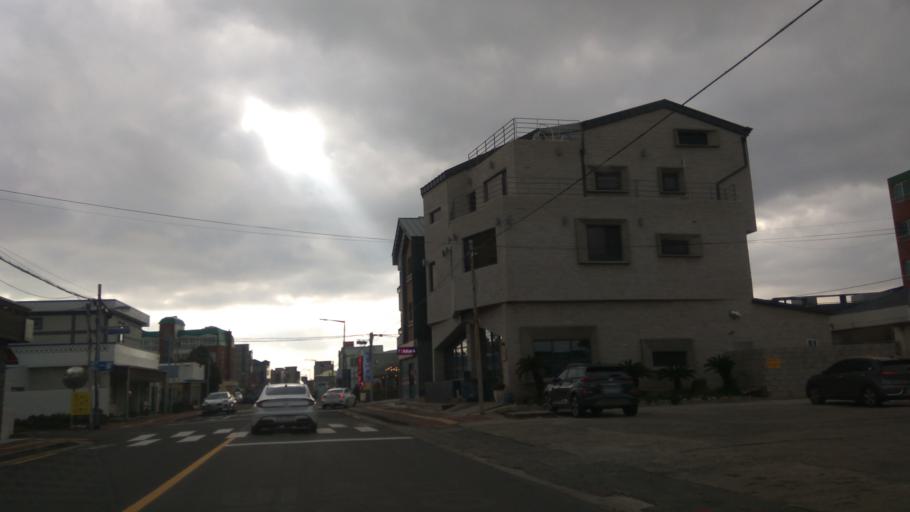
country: KR
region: Jeju-do
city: Jeju-si
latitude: 33.4627
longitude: 126.9329
